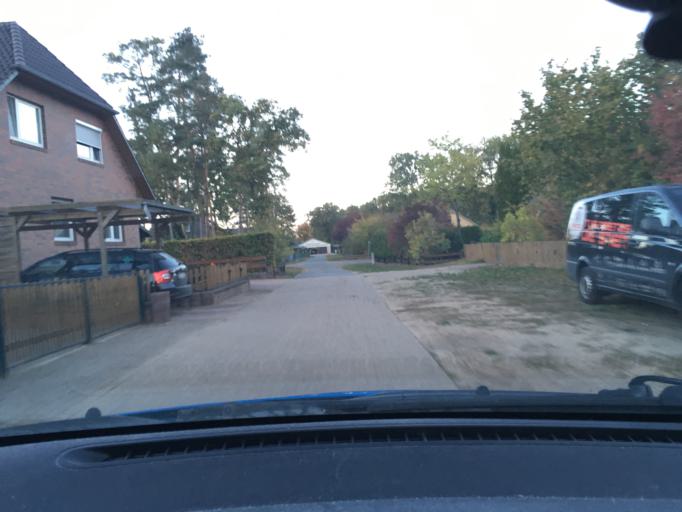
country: DE
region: Lower Saxony
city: Neetze
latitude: 53.2750
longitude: 10.6194
